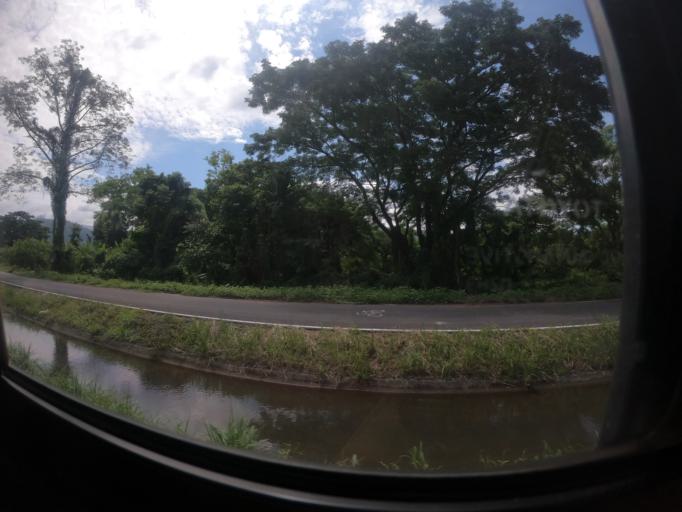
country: TH
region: Nakhon Nayok
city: Nakhon Nayok
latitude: 14.2991
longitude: 101.3059
